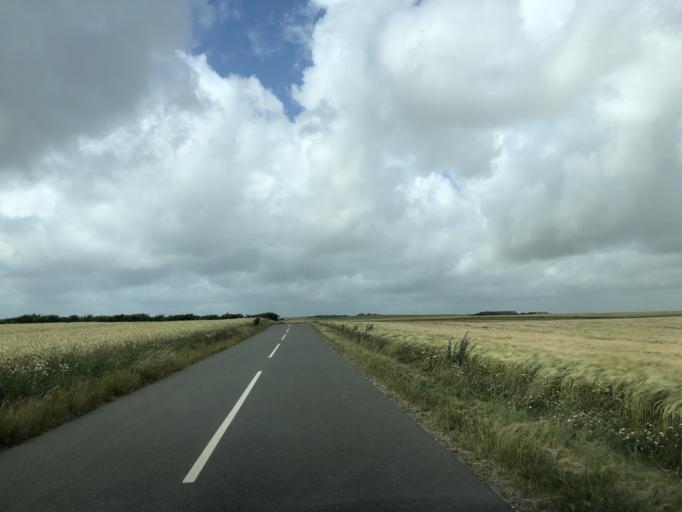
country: DK
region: Central Jutland
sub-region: Lemvig Kommune
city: Harboore
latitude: 56.4939
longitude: 8.1327
